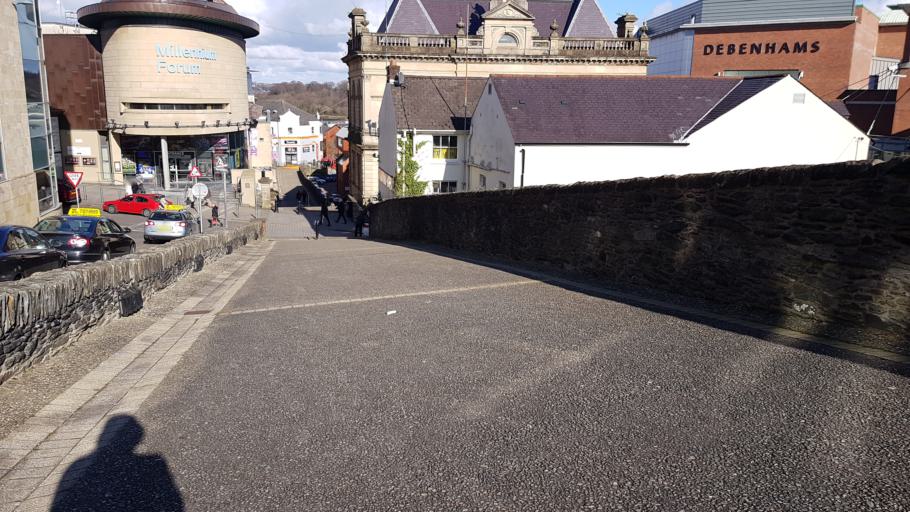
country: GB
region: Northern Ireland
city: Londonderry County Borough
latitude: 54.9950
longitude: -7.3197
